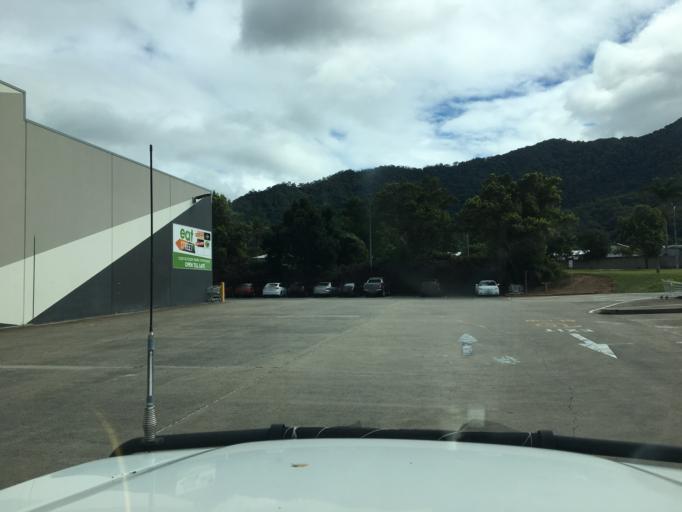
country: AU
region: Queensland
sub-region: Cairns
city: Woree
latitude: -16.9882
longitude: 145.7405
